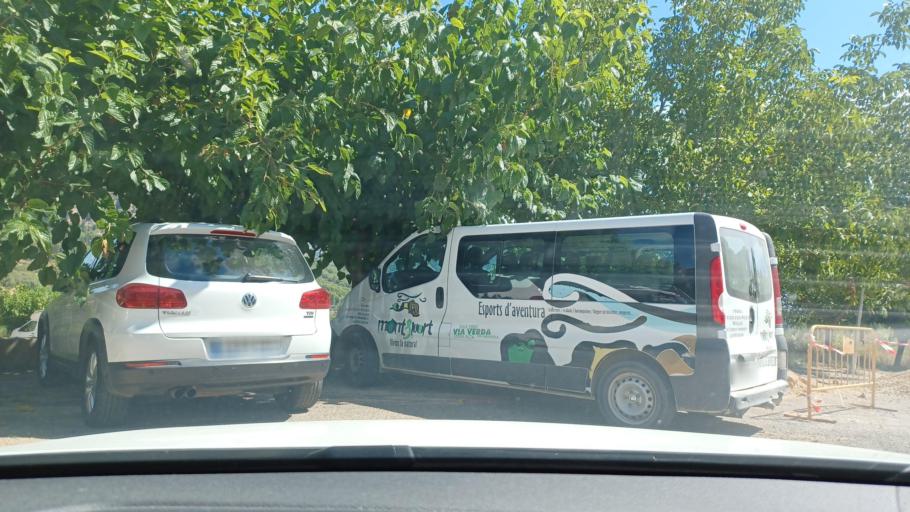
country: ES
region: Catalonia
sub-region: Provincia de Tarragona
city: Horta de Sant Joan
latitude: 40.9556
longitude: 0.3168
